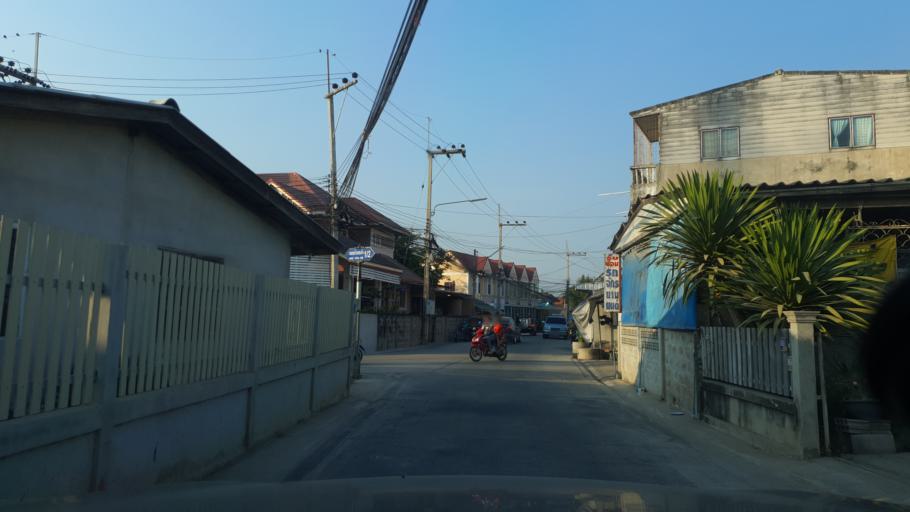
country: TH
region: Phetchaburi
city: Cha-am
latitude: 12.7952
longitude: 99.9640
